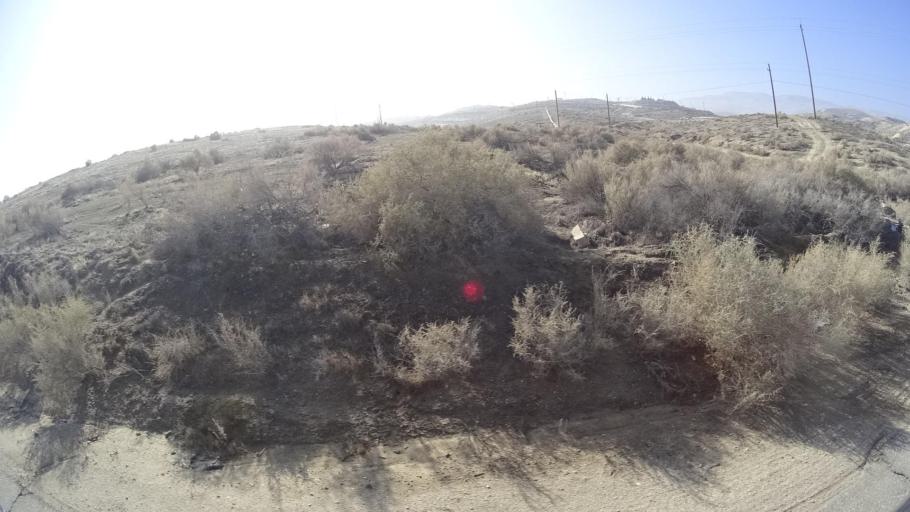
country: US
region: California
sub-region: Kern County
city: Taft Heights
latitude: 35.1410
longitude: -119.4983
